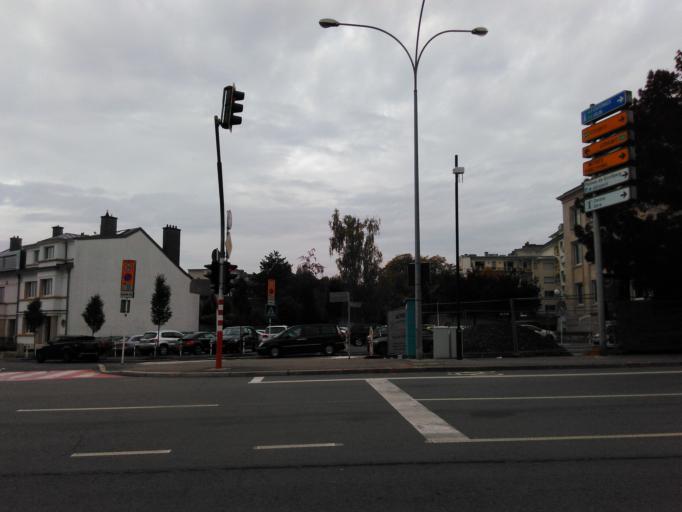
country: LU
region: Luxembourg
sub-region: Canton de Luxembourg
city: Luxembourg
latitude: 49.6058
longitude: 6.1198
